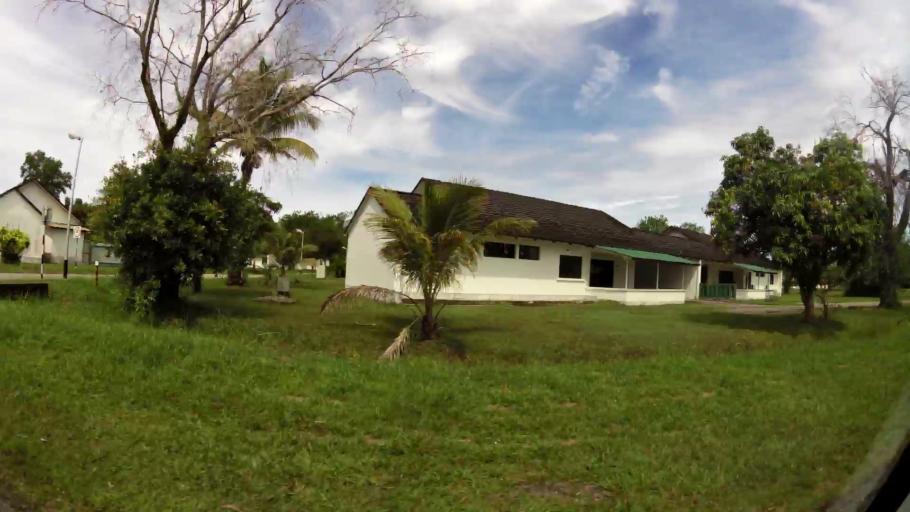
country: BN
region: Belait
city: Seria
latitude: 4.6030
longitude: 114.3096
